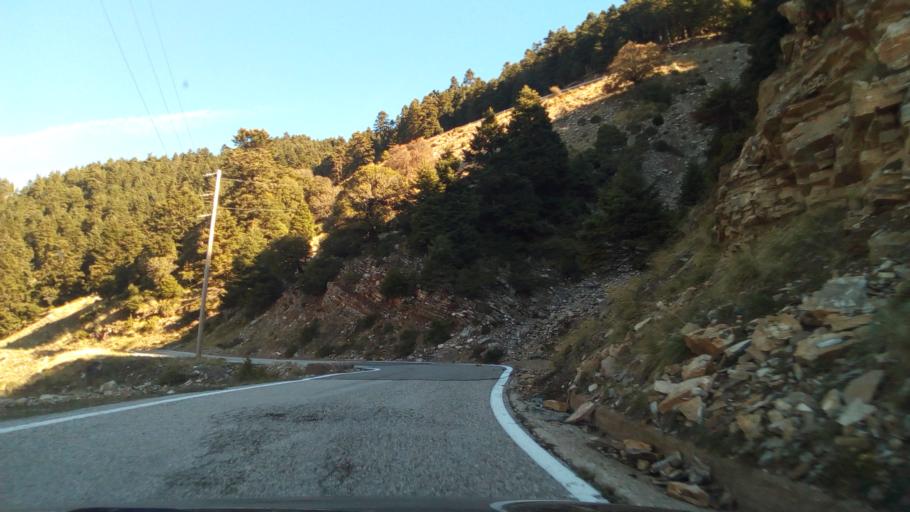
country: GR
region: West Greece
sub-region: Nomos Aitolias kai Akarnanias
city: Nafpaktos
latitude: 38.5269
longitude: 21.8478
